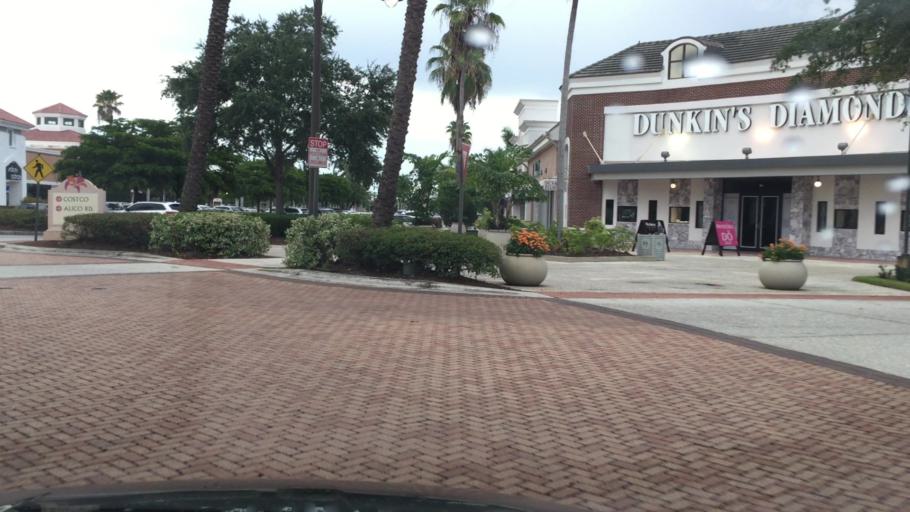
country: US
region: Florida
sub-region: Lee County
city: Three Oaks
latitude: 26.4866
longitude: -81.7878
